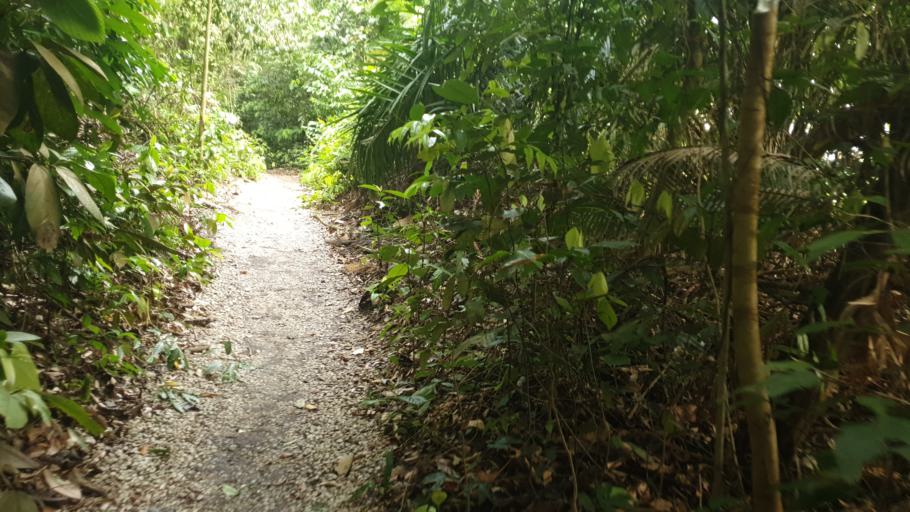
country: SG
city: Singapore
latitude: 1.3401
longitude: 103.8158
